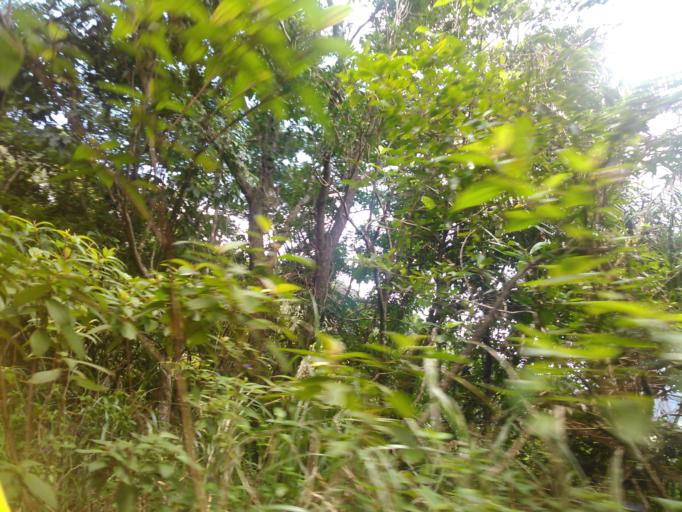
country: TW
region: Taiwan
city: Hengchun
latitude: 22.2657
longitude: 120.8207
